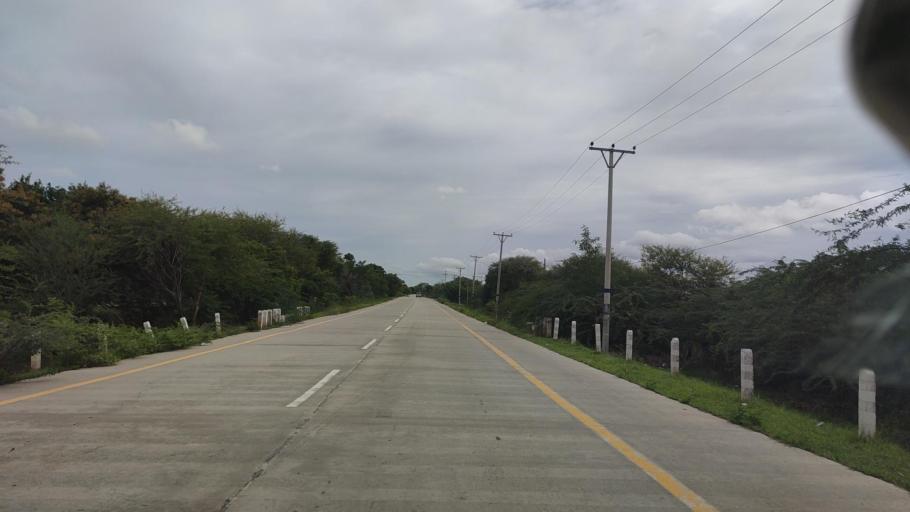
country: MM
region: Mandalay
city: Meiktila
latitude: 21.0762
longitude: 96.0065
